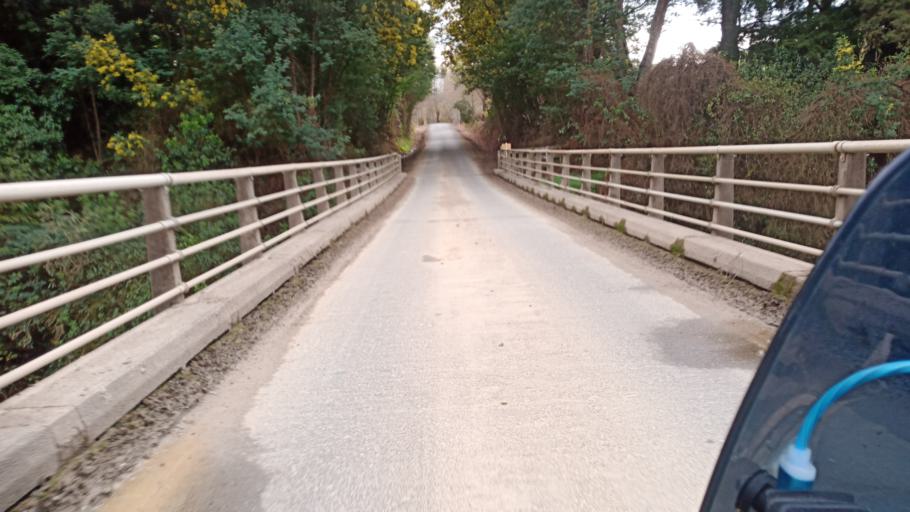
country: NZ
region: Hawke's Bay
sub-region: Wairoa District
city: Wairoa
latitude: -38.7727
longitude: 177.4157
